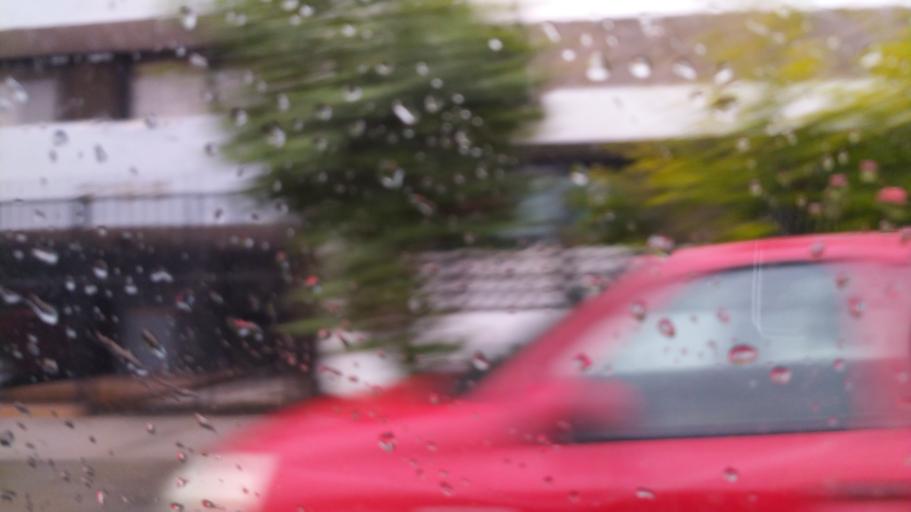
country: MX
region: Jalisco
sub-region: Zapopan
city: Zapopan
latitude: 20.7107
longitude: -103.3640
